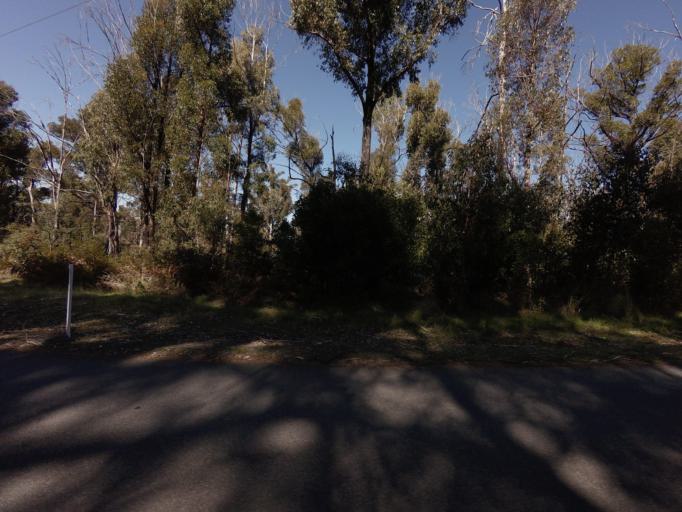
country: AU
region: Tasmania
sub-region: Derwent Valley
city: New Norfolk
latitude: -42.5530
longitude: 146.7129
